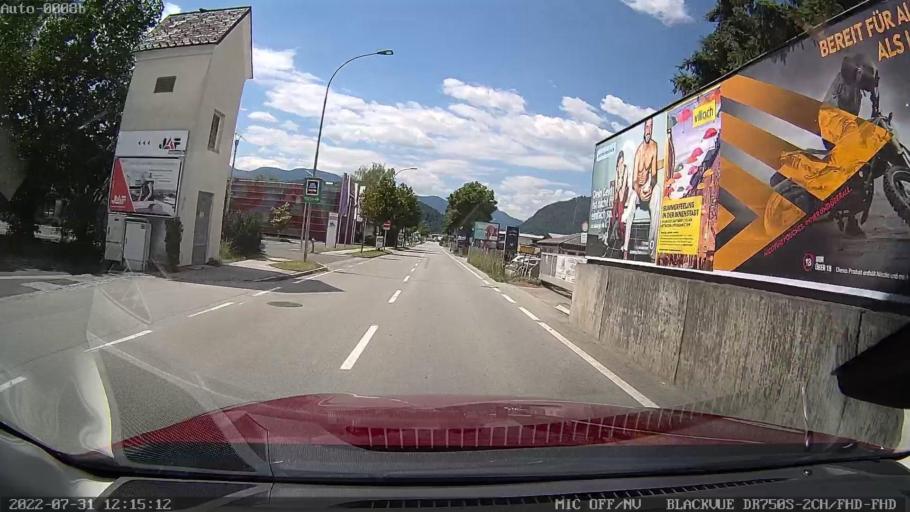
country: AT
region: Carinthia
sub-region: Villach Stadt
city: Villach
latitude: 46.5941
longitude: 13.8434
